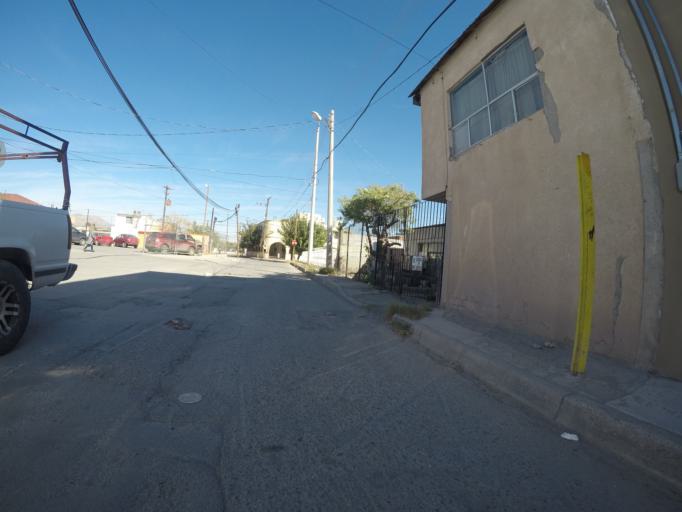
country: MX
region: Chihuahua
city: Ciudad Juarez
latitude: 31.7390
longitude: -106.4368
